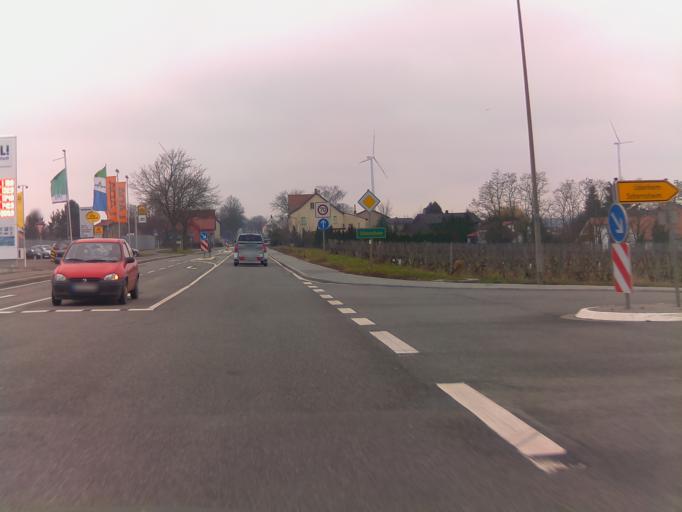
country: DE
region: Rheinland-Pfalz
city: Schornsheim
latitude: 49.8430
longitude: 8.1757
